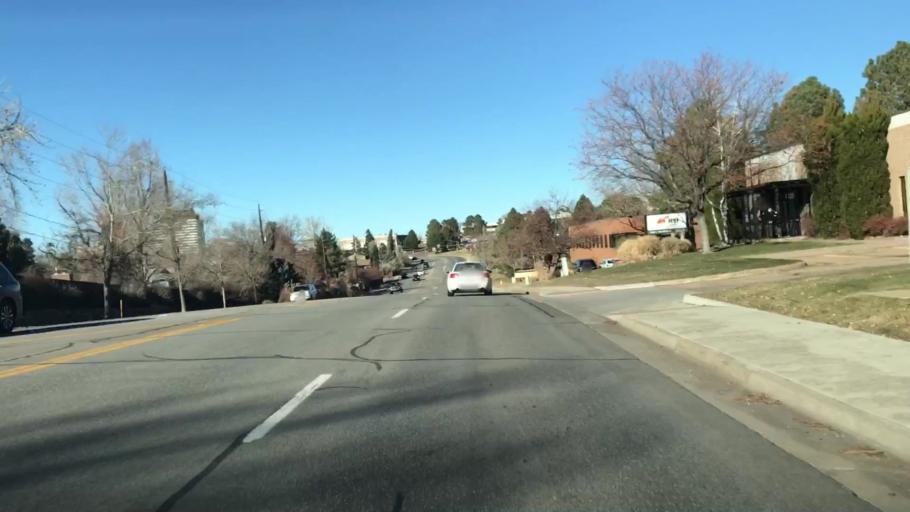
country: US
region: Colorado
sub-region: Arapahoe County
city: Centennial
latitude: 39.5877
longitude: -104.8853
